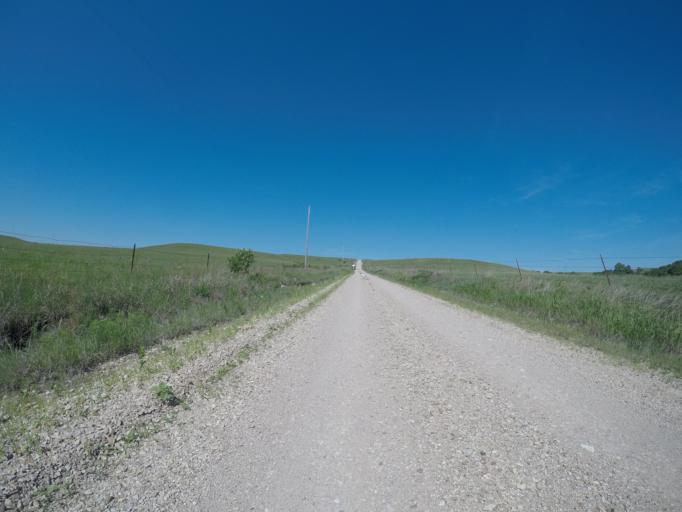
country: US
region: Kansas
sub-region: Wabaunsee County
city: Alma
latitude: 39.0152
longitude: -96.1619
